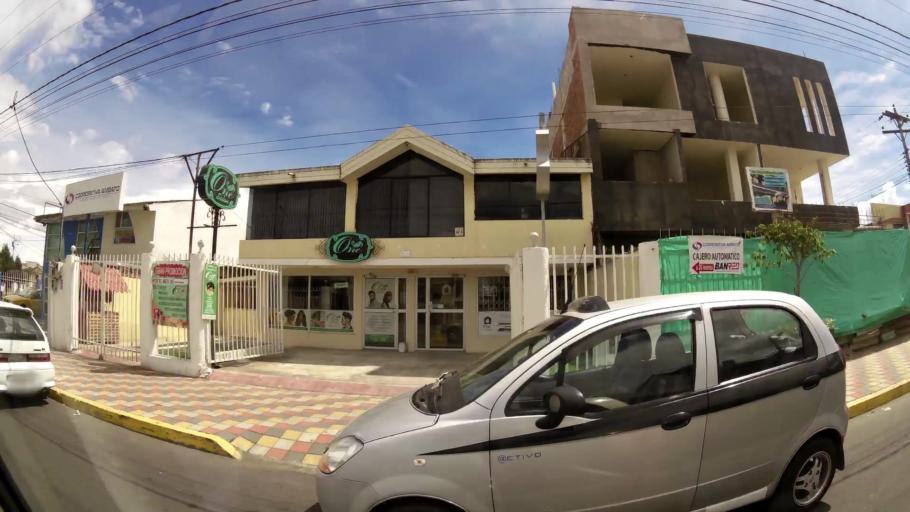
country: EC
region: Tungurahua
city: Ambato
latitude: -1.2613
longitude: -78.6248
